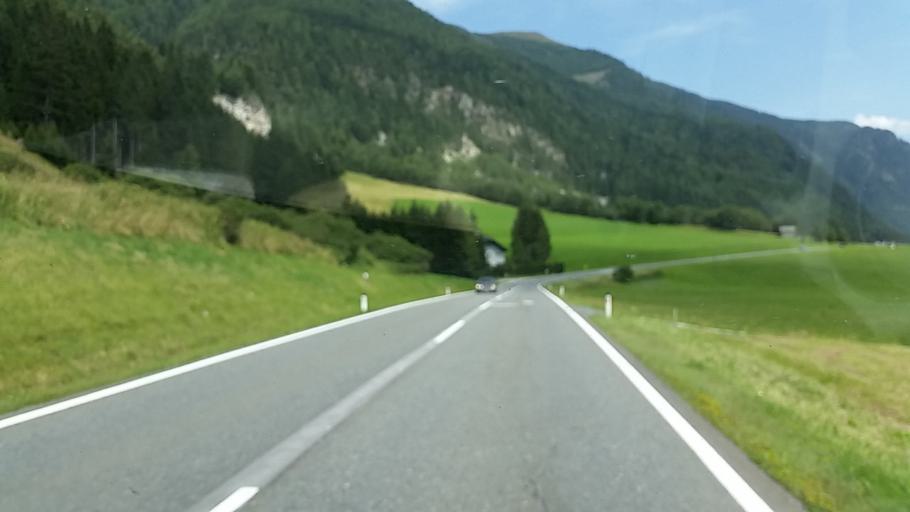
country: AT
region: Salzburg
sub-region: Politischer Bezirk Tamsweg
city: Tweng
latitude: 47.1837
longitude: 13.6168
